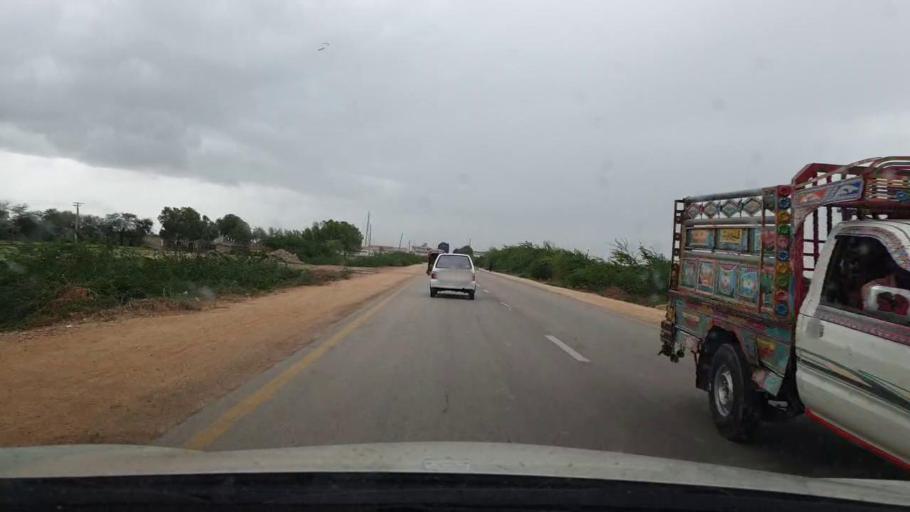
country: PK
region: Sindh
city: Kario
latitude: 24.6531
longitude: 68.5181
